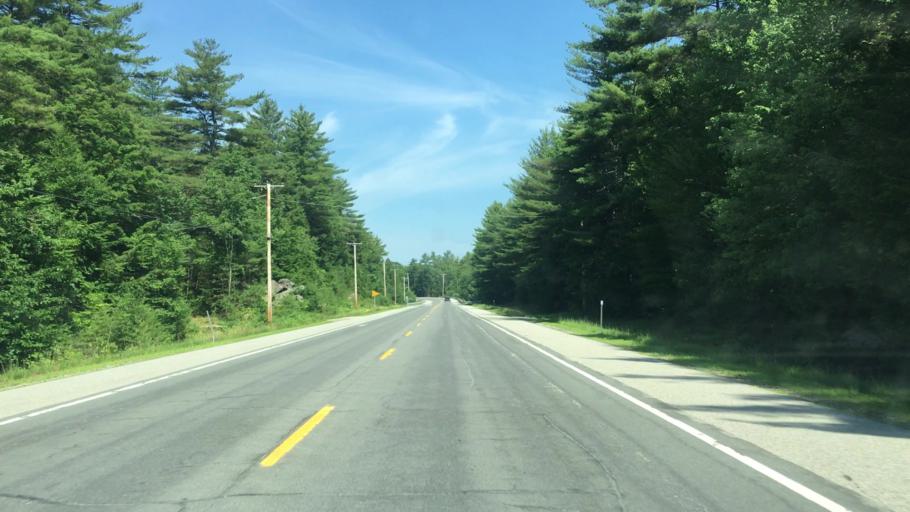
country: US
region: New Hampshire
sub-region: Merrimack County
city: Henniker
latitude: 43.2142
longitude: -71.8691
